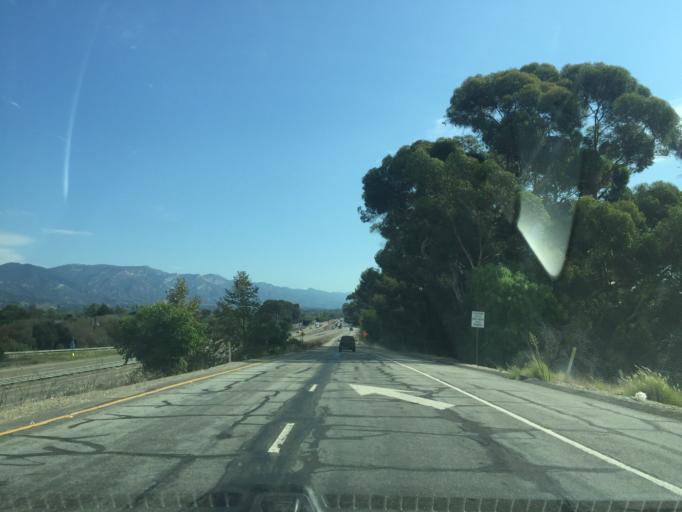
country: US
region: California
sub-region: Santa Barbara County
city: Goleta
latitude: 34.4375
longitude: -119.8521
